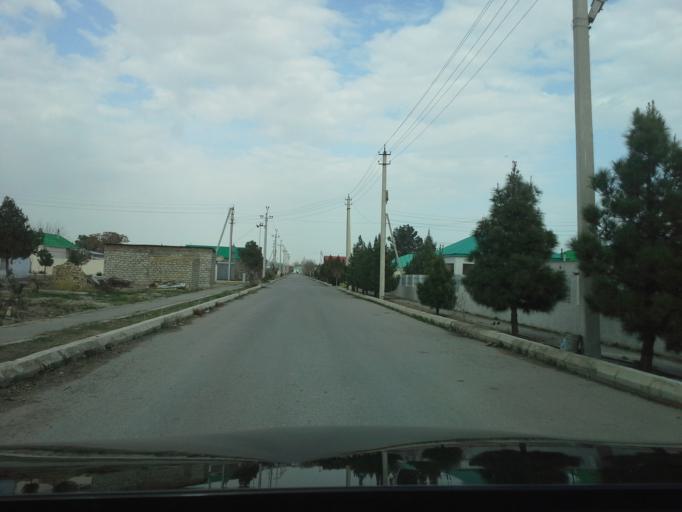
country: TM
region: Ahal
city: Ashgabat
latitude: 37.9848
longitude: 58.2854
